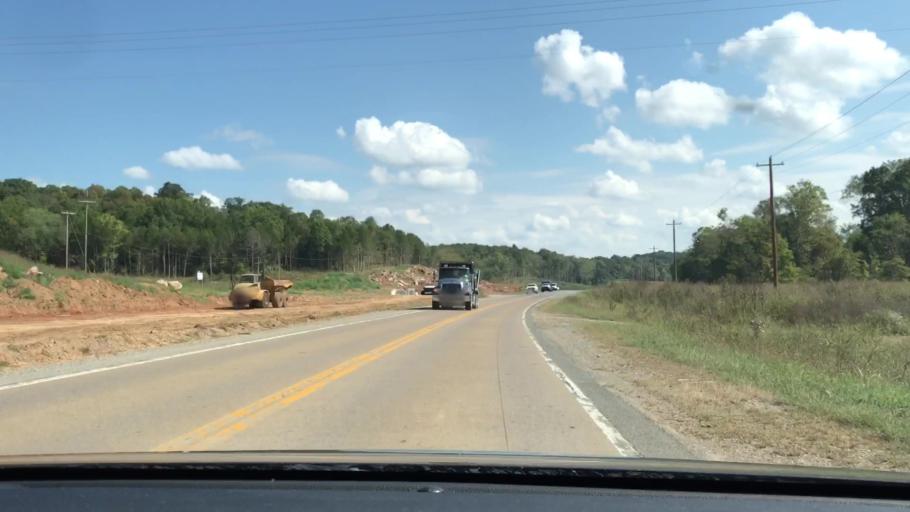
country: US
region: Kentucky
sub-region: Trigg County
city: Cadiz
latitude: 36.8041
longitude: -87.9338
